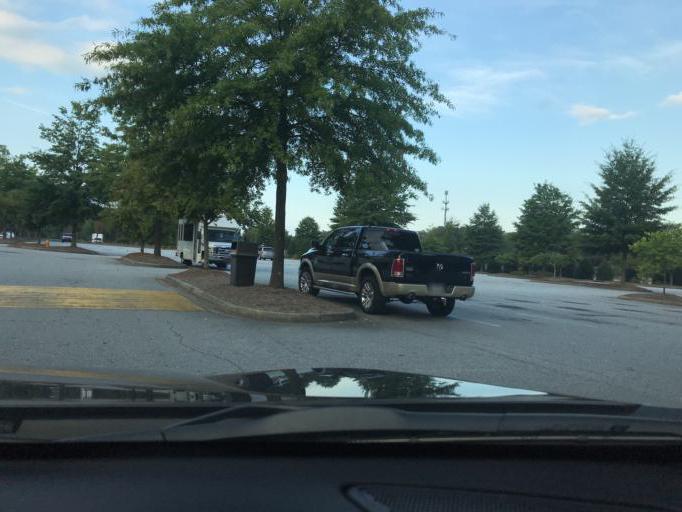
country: US
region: South Carolina
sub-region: Greenville County
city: Greenville
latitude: 34.8385
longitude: -82.3642
